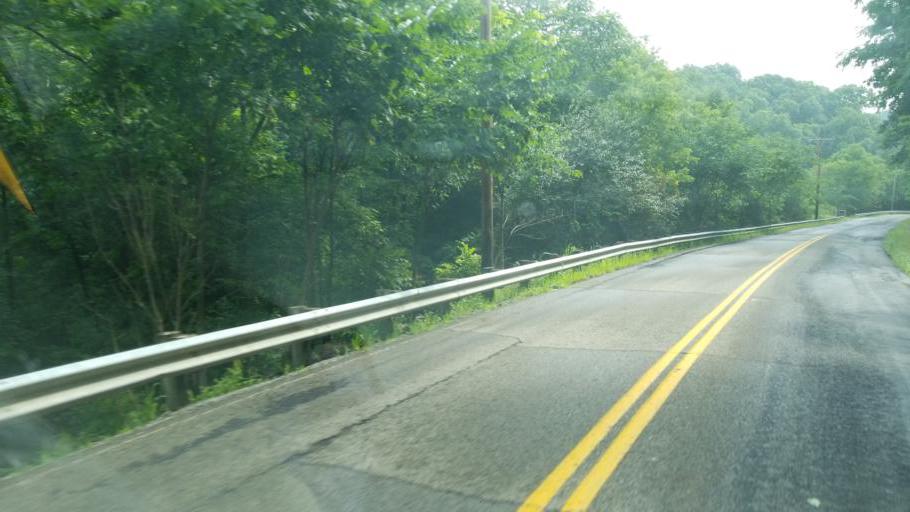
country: US
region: Ohio
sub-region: Columbiana County
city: Salineville
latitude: 40.5197
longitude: -80.8446
